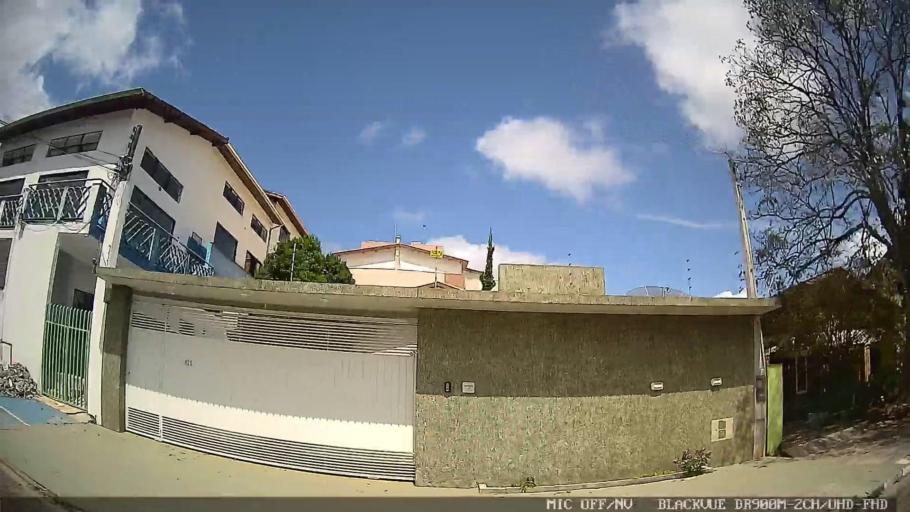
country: BR
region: Sao Paulo
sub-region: Caraguatatuba
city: Caraguatatuba
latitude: -23.6313
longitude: -45.4195
